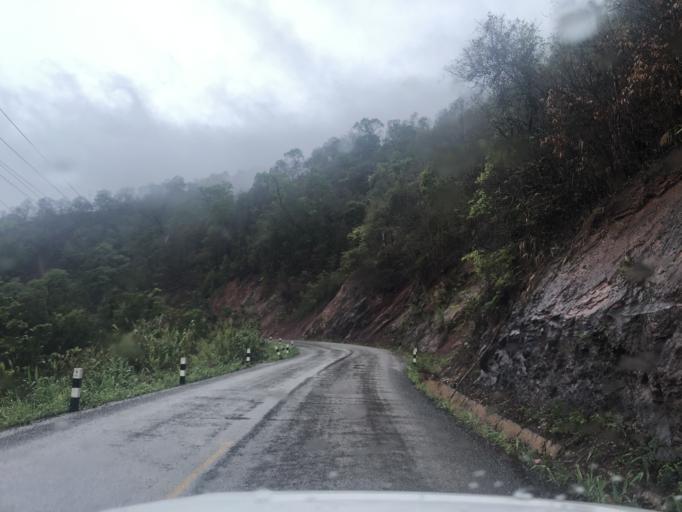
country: LA
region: Phongsali
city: Phongsali
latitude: 21.6718
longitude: 101.8802
